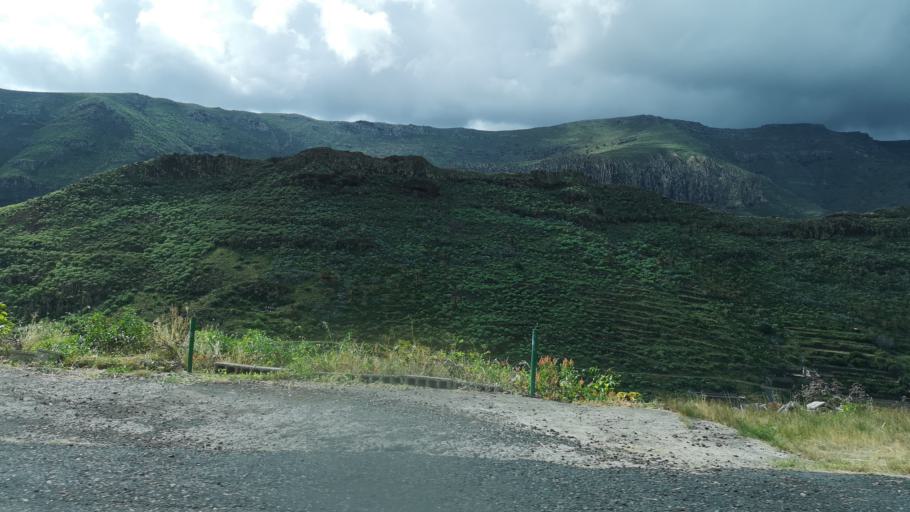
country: ES
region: Canary Islands
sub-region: Provincia de Santa Cruz de Tenerife
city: San Sebastian de la Gomera
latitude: 28.1121
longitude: -17.1326
